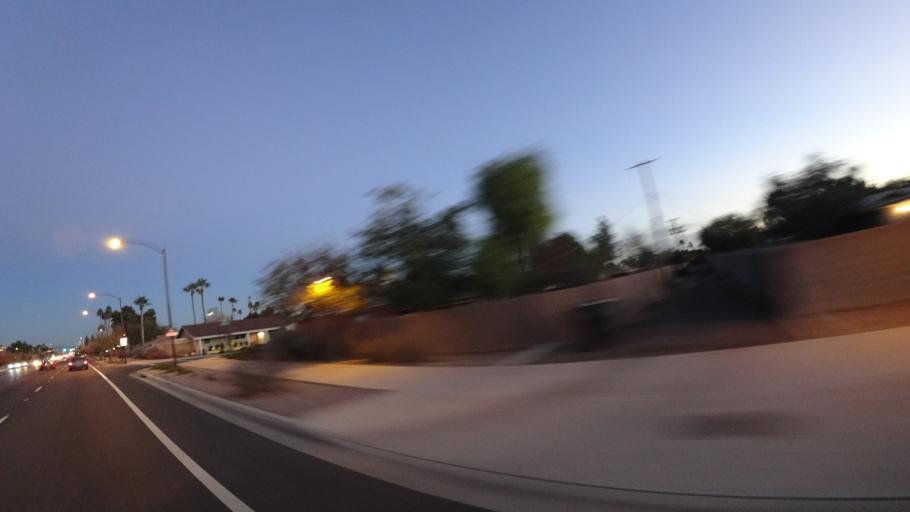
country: US
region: Arizona
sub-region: Maricopa County
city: Scottsdale
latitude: 33.4948
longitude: -111.9043
